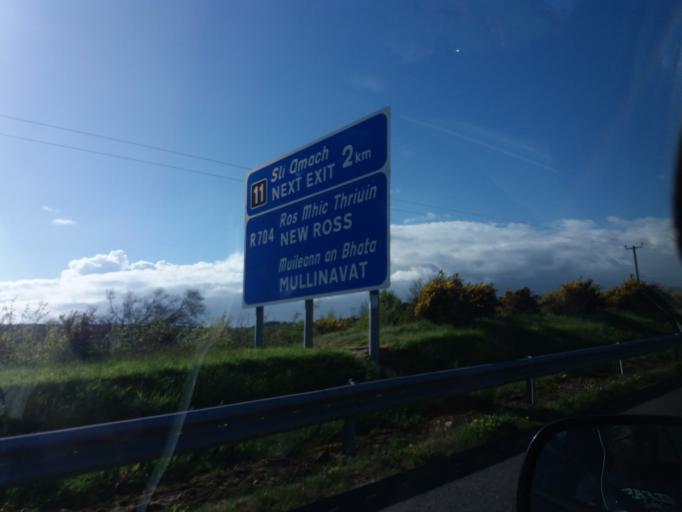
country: IE
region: Leinster
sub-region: Kilkenny
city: Mooncoin
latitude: 52.3493
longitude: -7.1674
